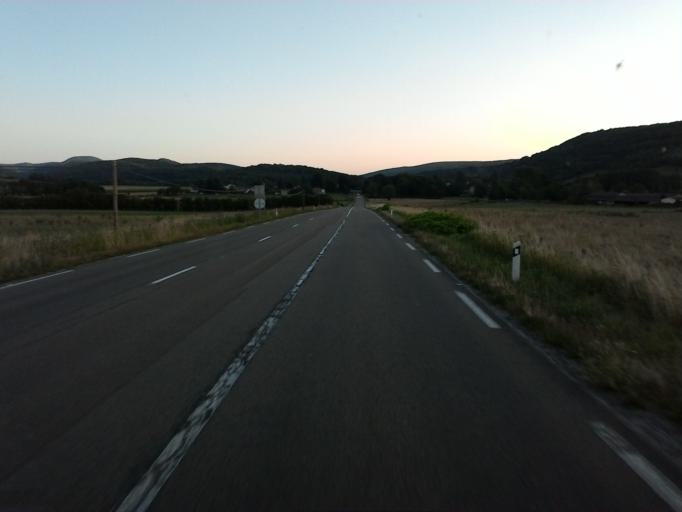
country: FR
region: Franche-Comte
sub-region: Departement du Jura
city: Salins-les-Bains
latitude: 47.0177
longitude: 5.8621
